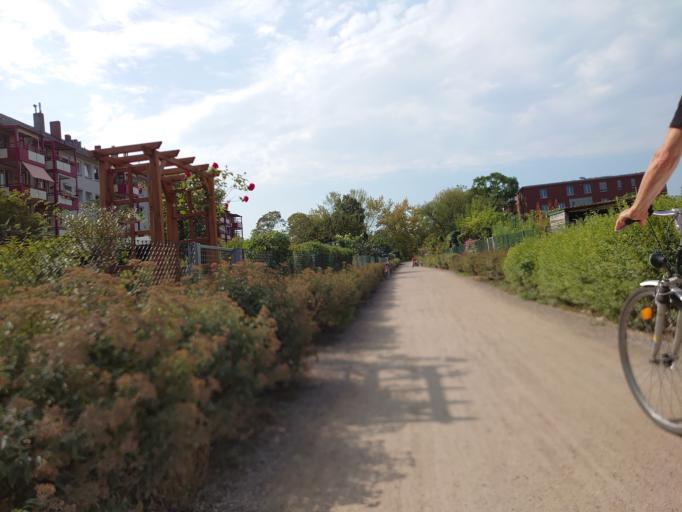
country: DE
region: North Rhine-Westphalia
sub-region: Regierungsbezirk Koln
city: Riehl
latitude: 50.9678
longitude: 6.9647
